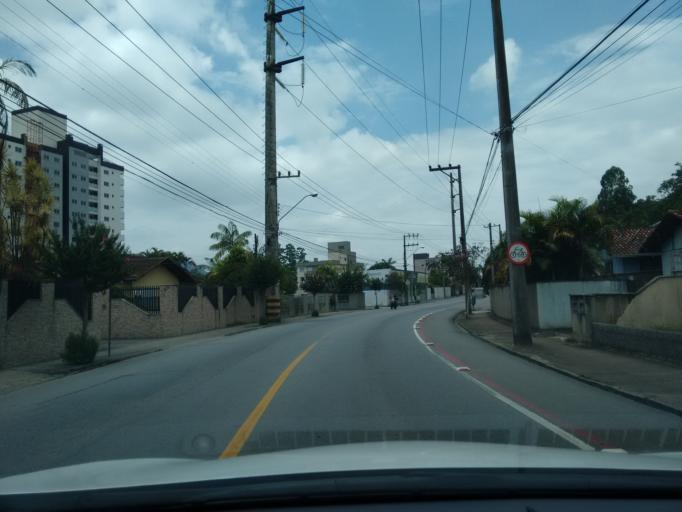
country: BR
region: Santa Catarina
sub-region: Jaragua Do Sul
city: Jaragua do Sul
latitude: -26.4965
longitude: -49.0803
